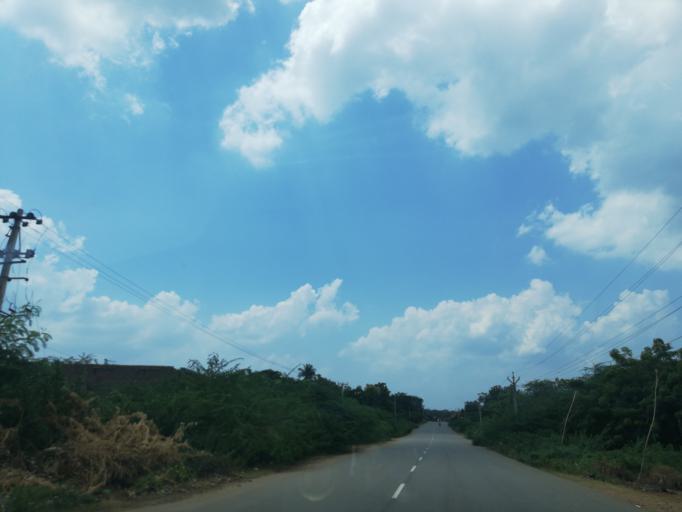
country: IN
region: Andhra Pradesh
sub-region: Guntur
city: Macherla
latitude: 16.5892
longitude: 79.3192
